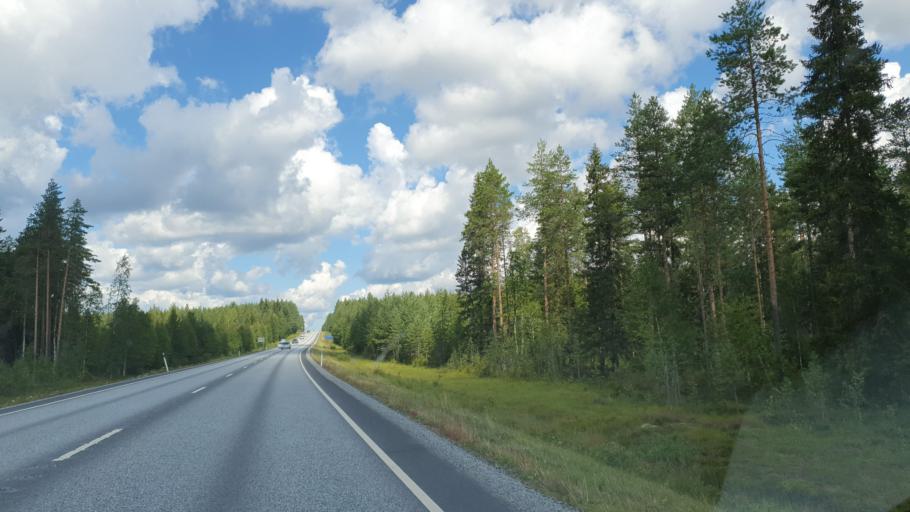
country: FI
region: Northern Savo
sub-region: Ylae-Savo
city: Sonkajaervi
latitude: 63.9139
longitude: 27.3840
